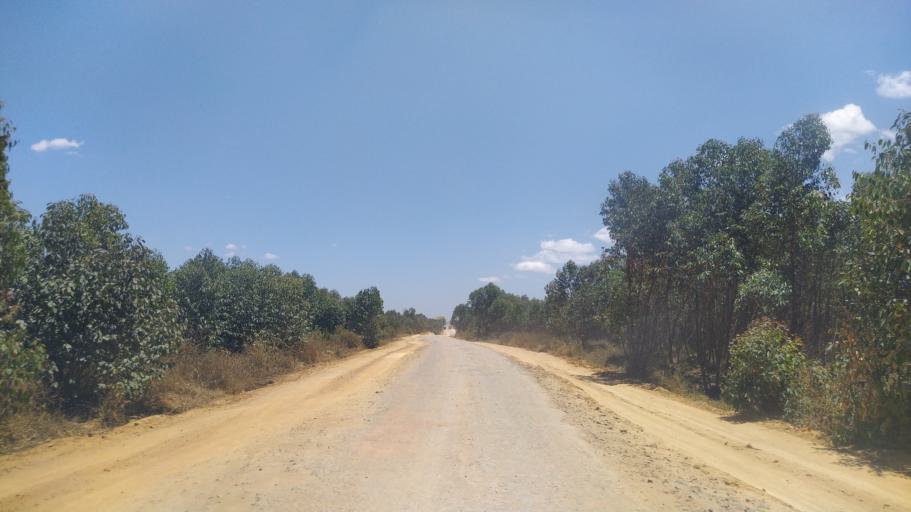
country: MG
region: Alaotra Mangoro
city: Moramanga
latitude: -18.6435
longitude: 48.2755
